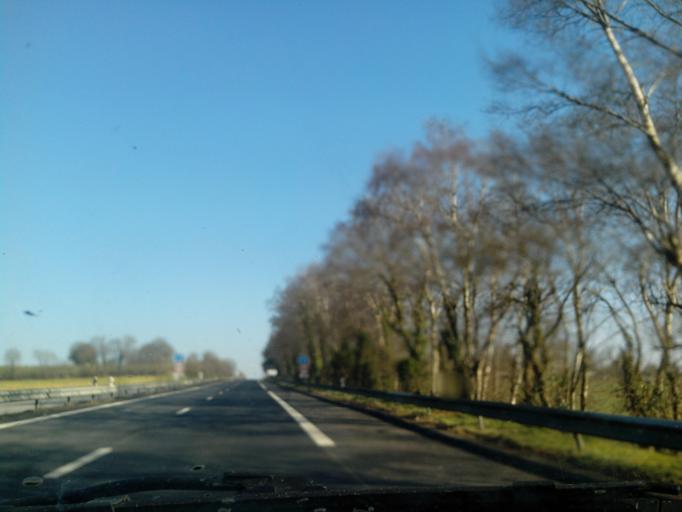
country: FR
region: Brittany
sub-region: Departement des Cotes-d'Armor
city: Plemet
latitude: 48.1695
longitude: -2.6262
